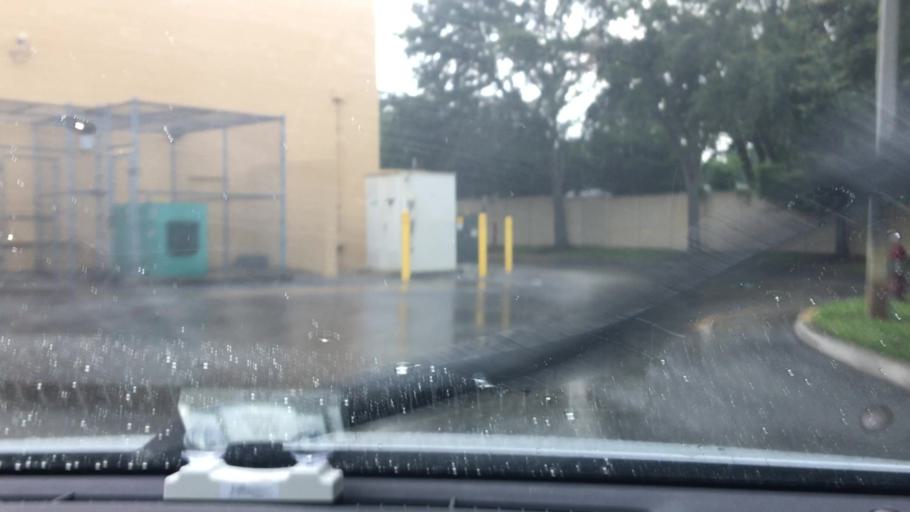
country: US
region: Florida
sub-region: Orange County
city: Conway
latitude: 28.4821
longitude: -81.3288
